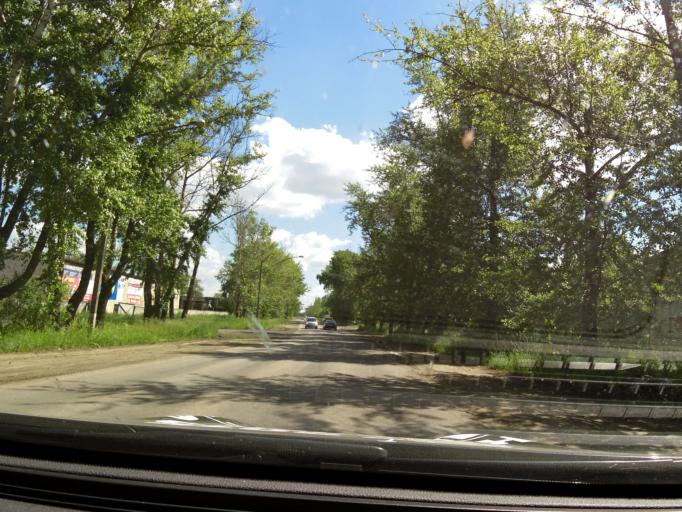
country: RU
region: Vologda
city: Vologda
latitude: 59.2367
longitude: 39.8235
